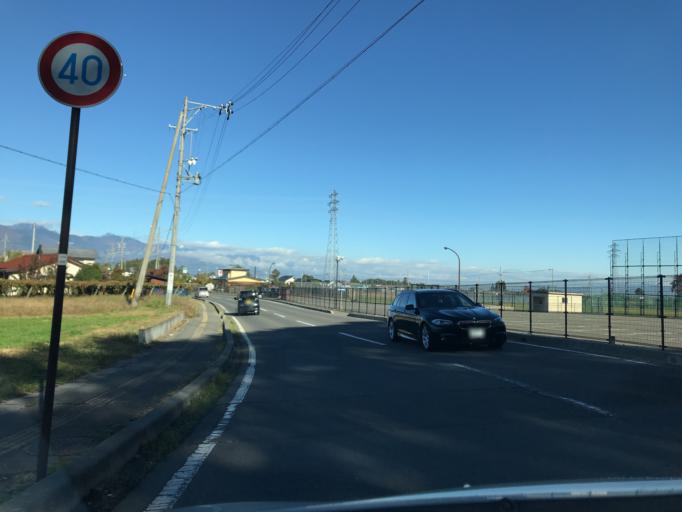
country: JP
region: Nagano
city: Shiojiri
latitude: 36.1269
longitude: 137.9377
